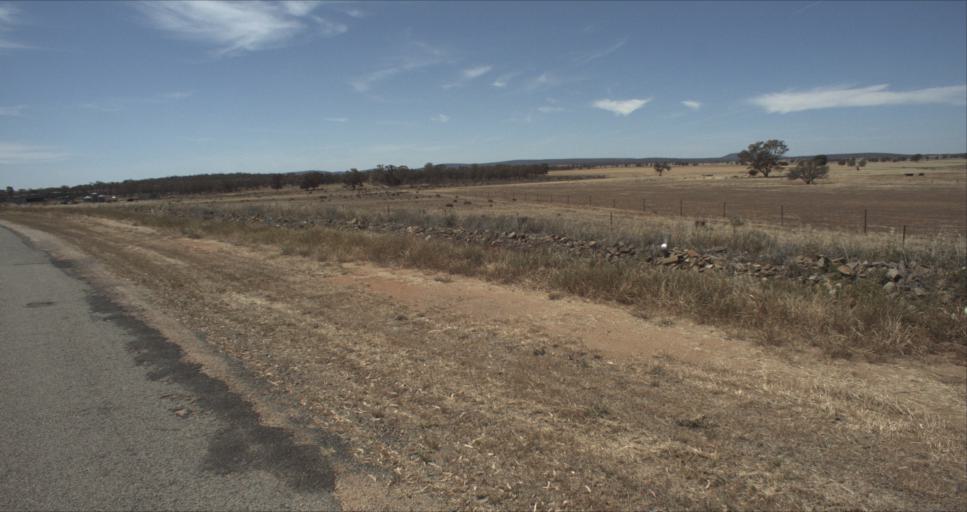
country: AU
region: New South Wales
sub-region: Leeton
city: Leeton
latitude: -34.6012
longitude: 146.4795
